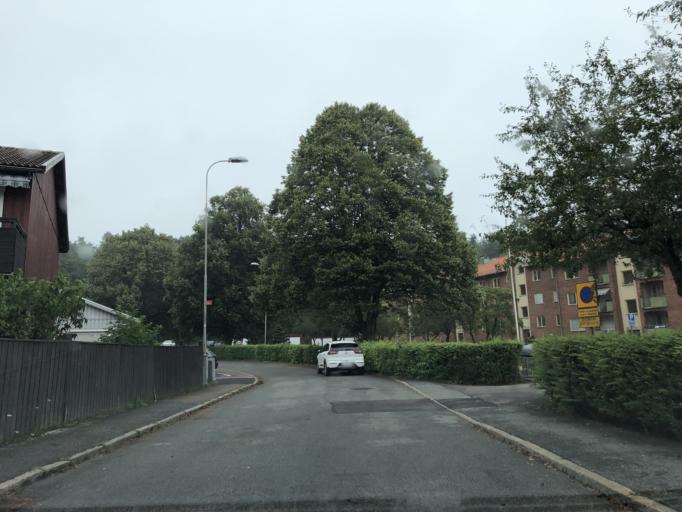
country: SE
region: Vaestra Goetaland
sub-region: Goteborg
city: Goeteborg
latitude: 57.7313
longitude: 11.9342
